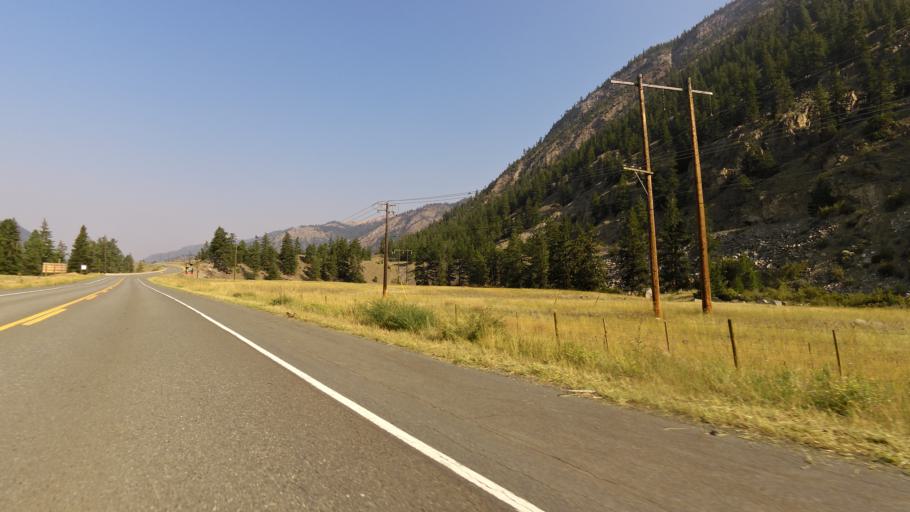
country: CA
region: British Columbia
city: Princeton
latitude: 49.3421
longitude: -120.0625
